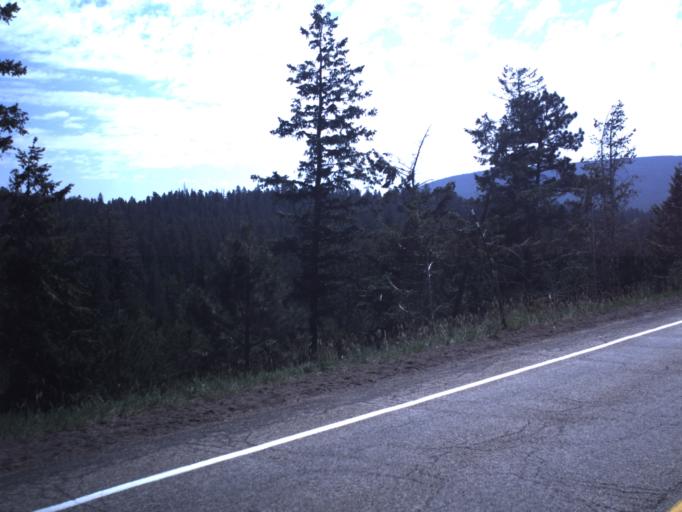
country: US
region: Utah
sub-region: Daggett County
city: Manila
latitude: 40.8474
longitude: -109.6674
